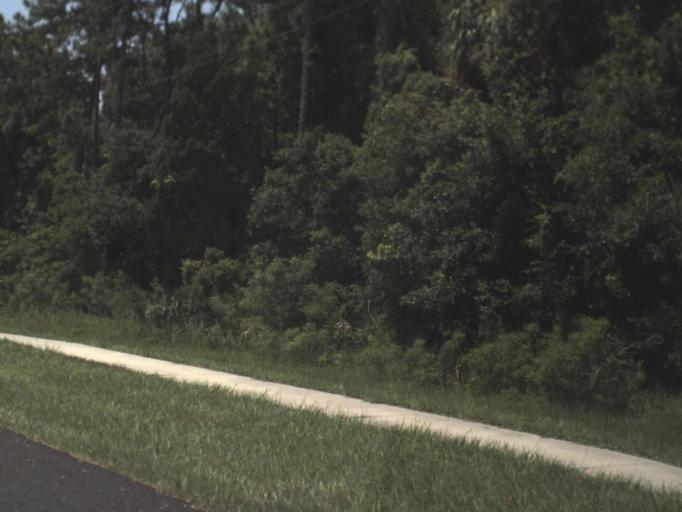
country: US
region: Florida
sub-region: Citrus County
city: Crystal River
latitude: 28.9105
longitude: -82.6060
